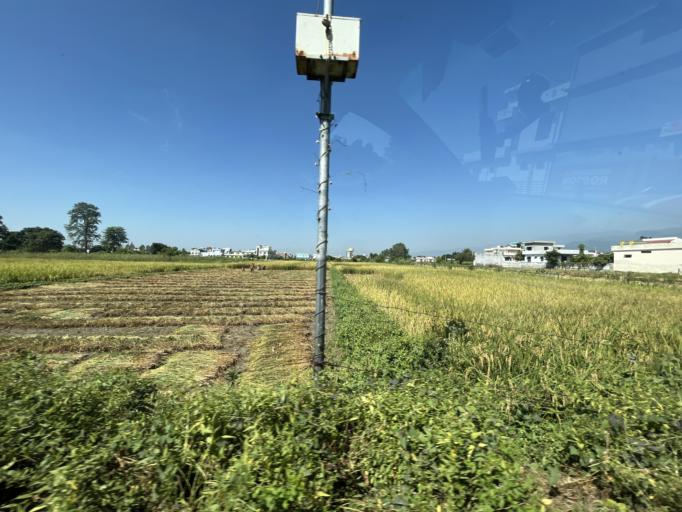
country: IN
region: Uttarakhand
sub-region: Naini Tal
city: Haldwani
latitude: 29.2096
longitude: 79.4944
